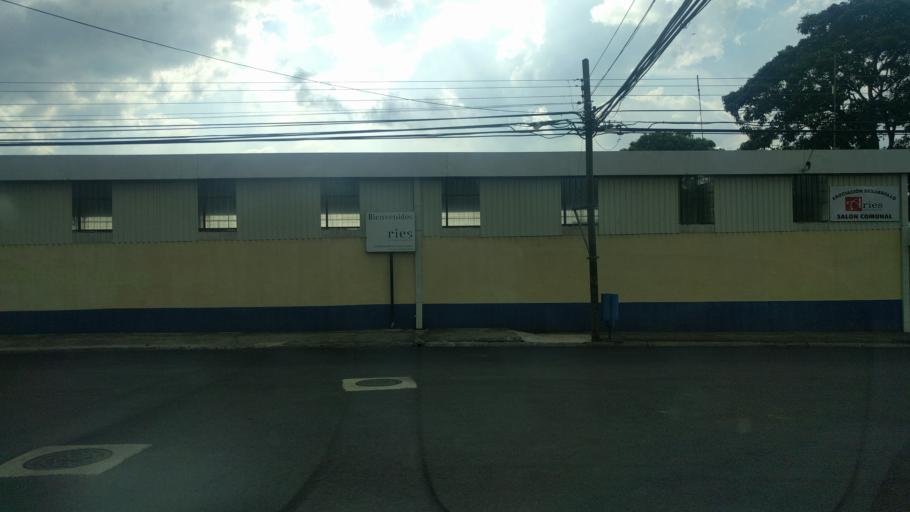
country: CR
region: Heredia
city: Llorente
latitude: 9.9948
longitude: -84.1486
